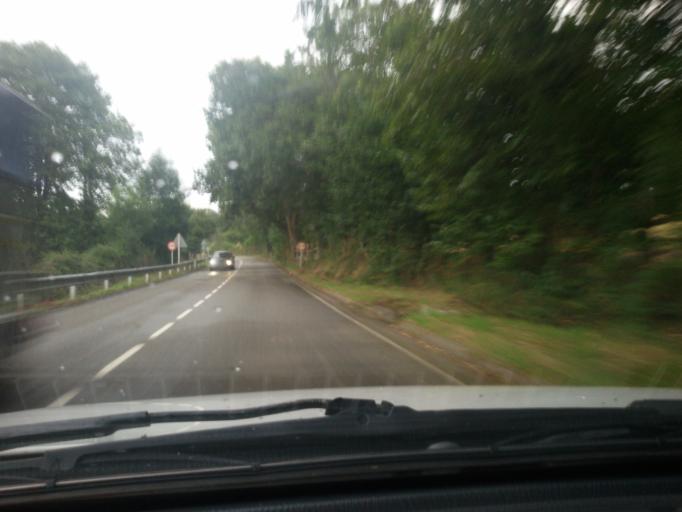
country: ES
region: Asturias
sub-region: Province of Asturias
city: Norena
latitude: 43.3738
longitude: -5.7205
